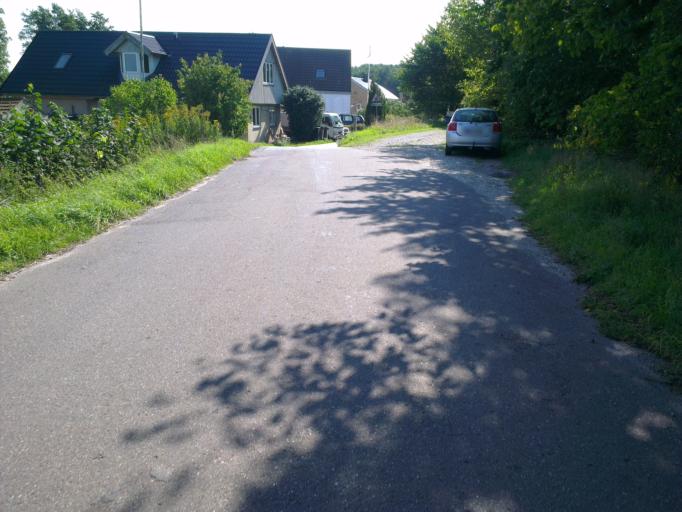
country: DK
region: Capital Region
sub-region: Frederikssund Kommune
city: Frederikssund
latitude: 55.8351
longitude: 12.0323
